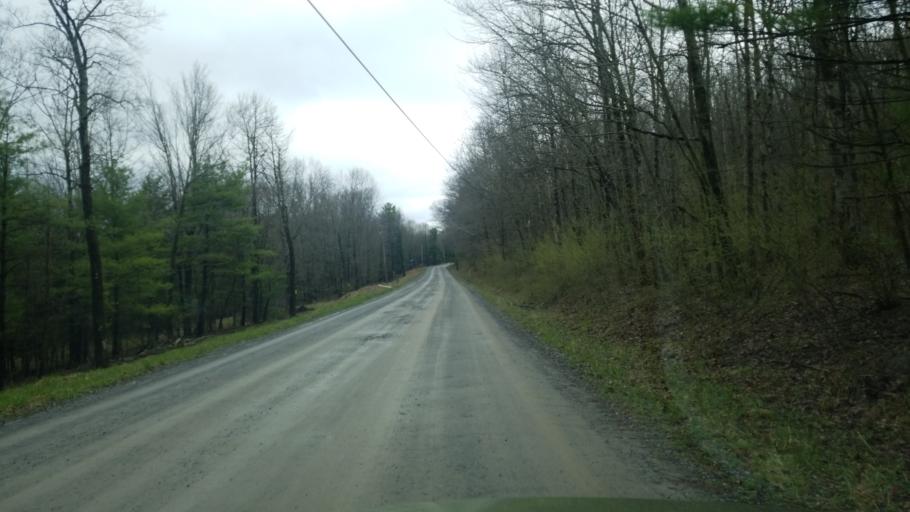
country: US
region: Pennsylvania
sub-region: Clearfield County
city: Shiloh
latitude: 41.1335
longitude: -78.3348
